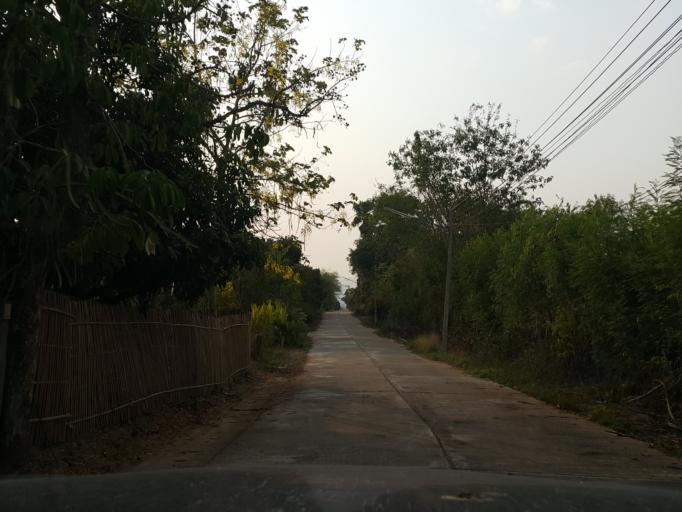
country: TH
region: Lamphun
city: Li
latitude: 17.8093
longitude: 98.9485
